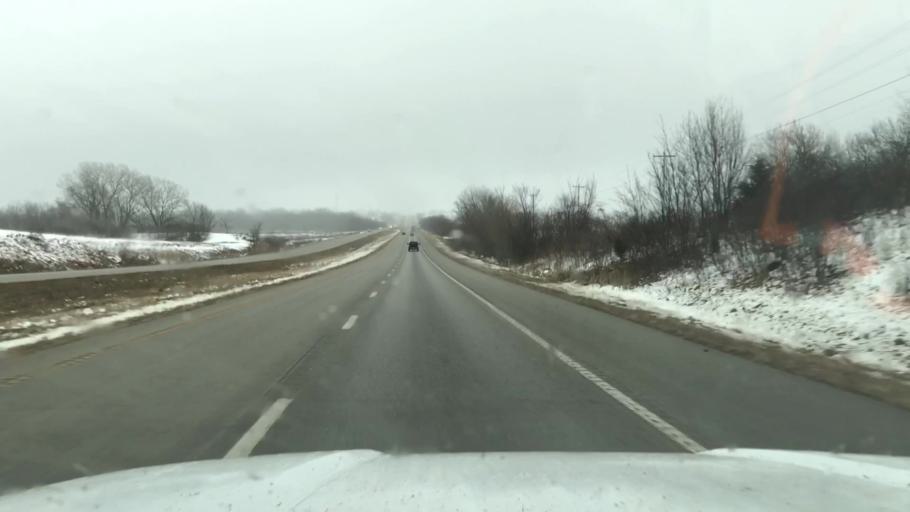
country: US
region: Missouri
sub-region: Clinton County
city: Gower
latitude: 39.7474
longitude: -94.6734
